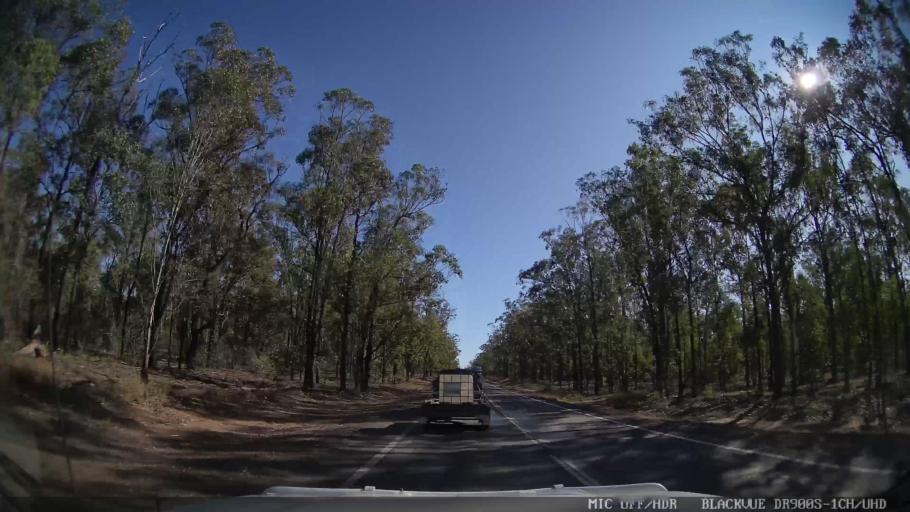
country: AU
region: Queensland
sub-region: Bundaberg
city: Childers
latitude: -25.2166
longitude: 152.0724
